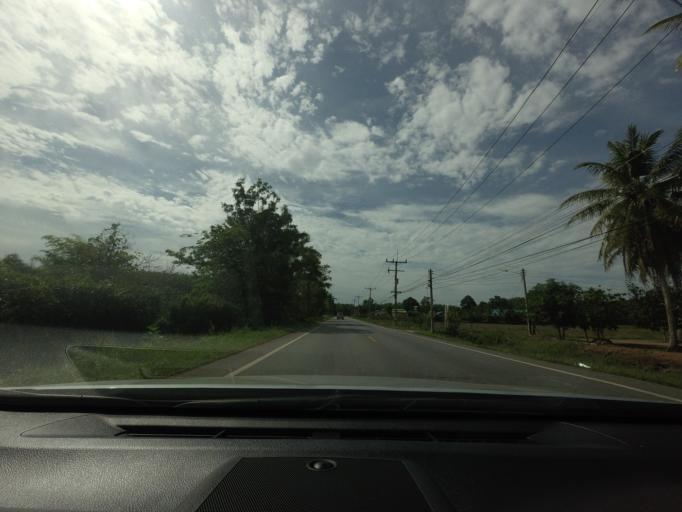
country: TH
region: Songkhla
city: Khlong Hoi Khong
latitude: 6.8909
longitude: 100.4150
